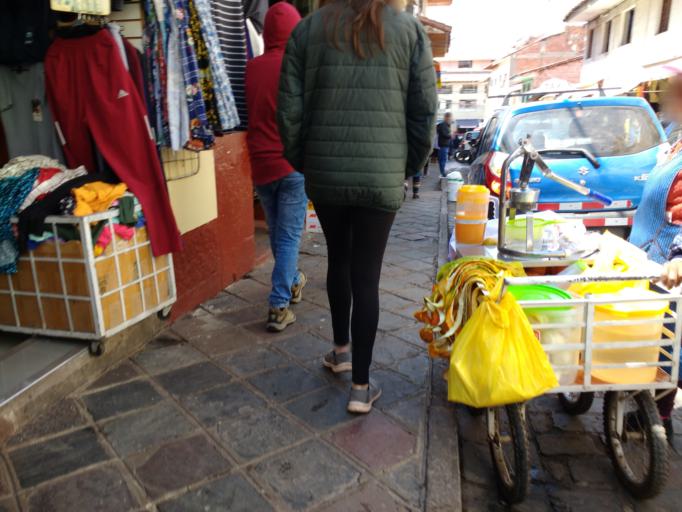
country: PE
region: Cusco
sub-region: Provincia de Cusco
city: Cusco
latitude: -13.5223
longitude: -71.9813
